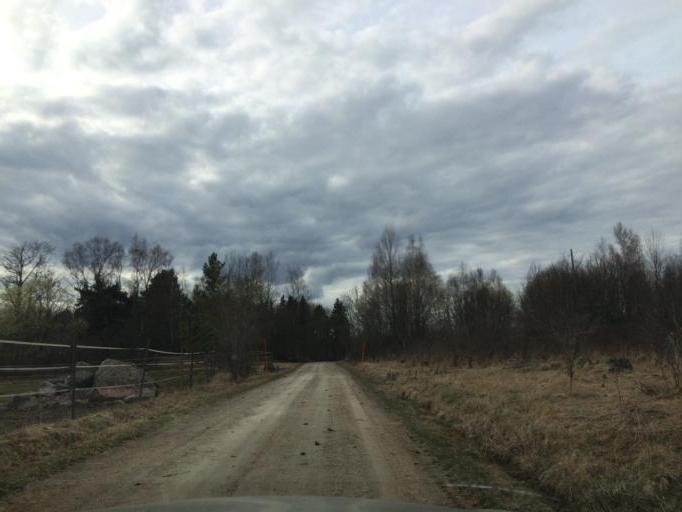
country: SE
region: Soedermanland
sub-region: Eskilstuna Kommun
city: Hallbybrunn
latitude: 59.4163
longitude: 16.3973
